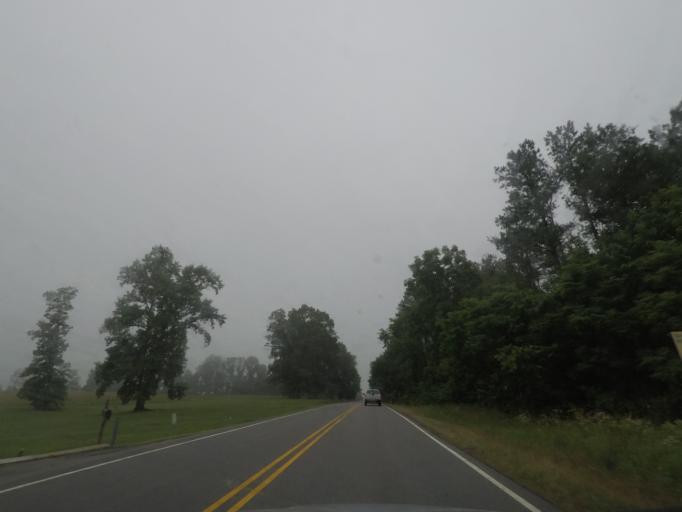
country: US
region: Virginia
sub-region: Prince Edward County
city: Farmville
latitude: 37.3472
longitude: -78.4758
